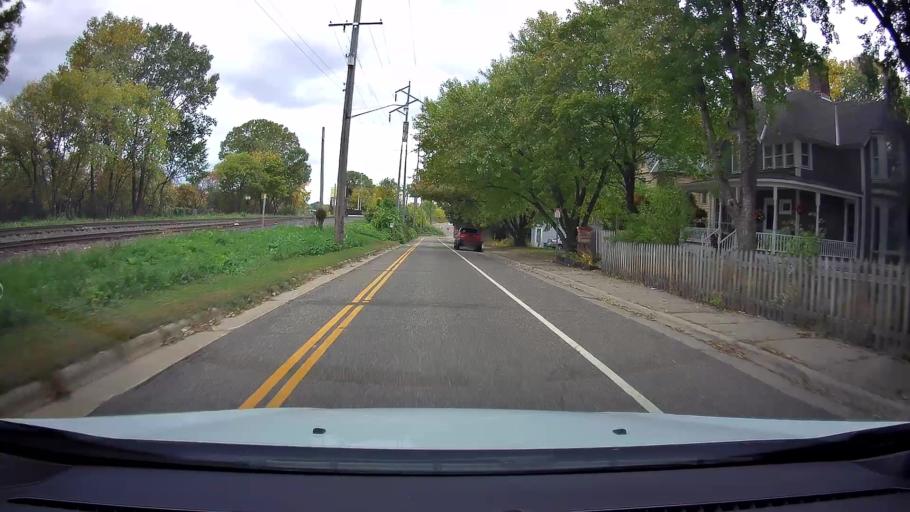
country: US
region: Minnesota
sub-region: Ramsey County
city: Falcon Heights
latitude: 44.9533
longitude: -93.1805
